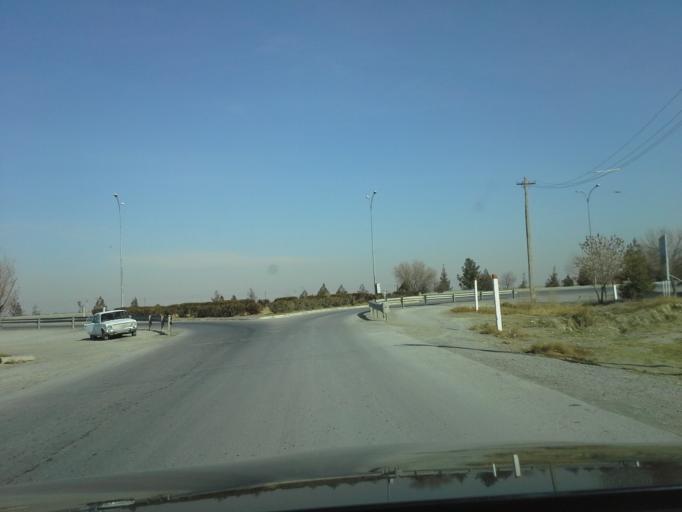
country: TM
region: Ahal
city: Abadan
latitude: 38.1359
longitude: 58.0073
